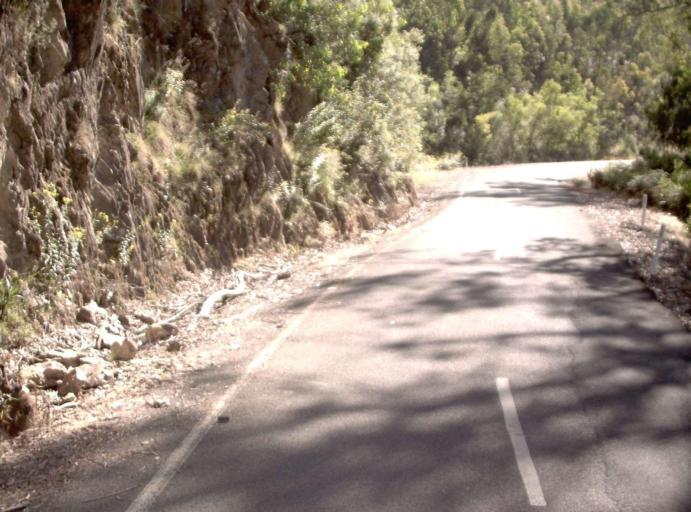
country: AU
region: Victoria
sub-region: East Gippsland
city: Lakes Entrance
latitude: -37.5199
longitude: 148.5387
